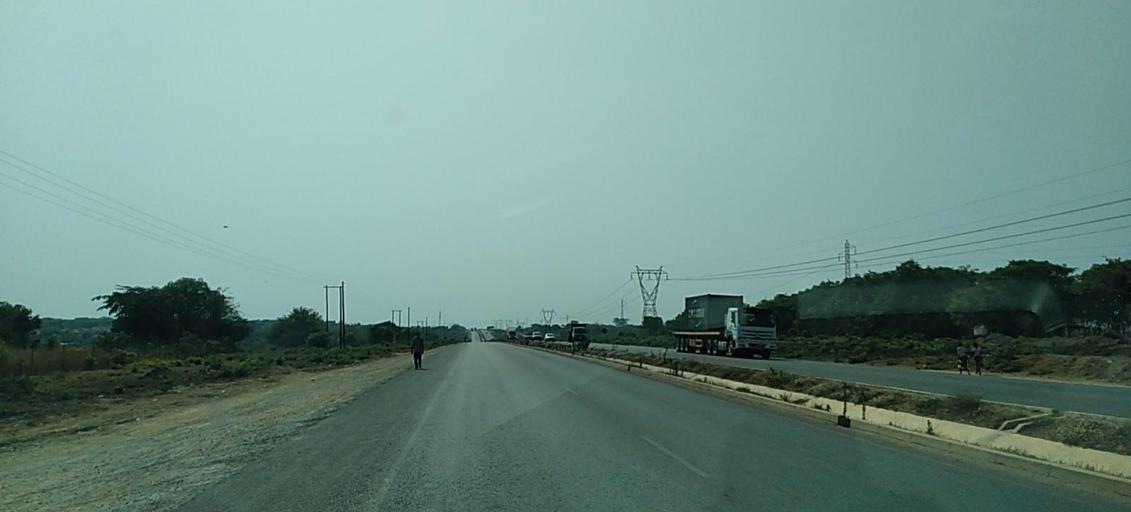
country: ZM
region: Copperbelt
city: Chingola
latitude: -12.5637
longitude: 27.8860
